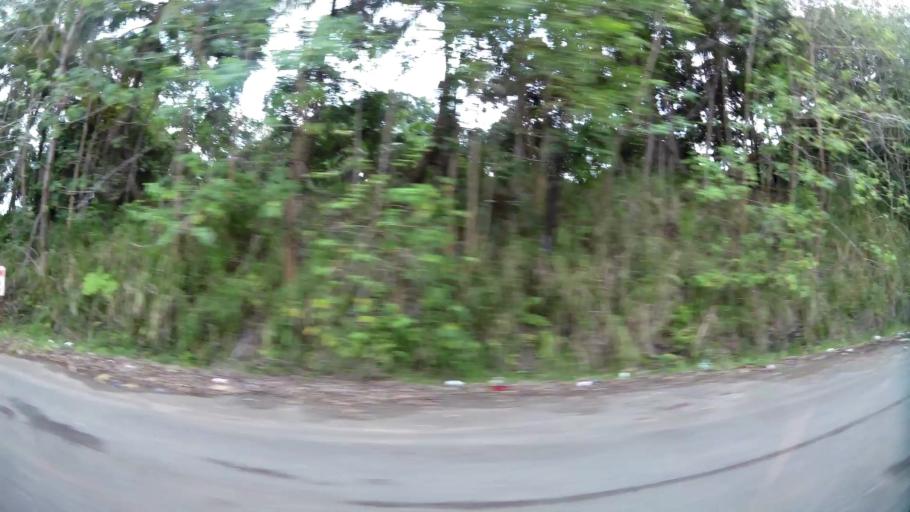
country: DO
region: San Cristobal
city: Villa Altagracia
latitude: 18.6489
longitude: -70.1694
